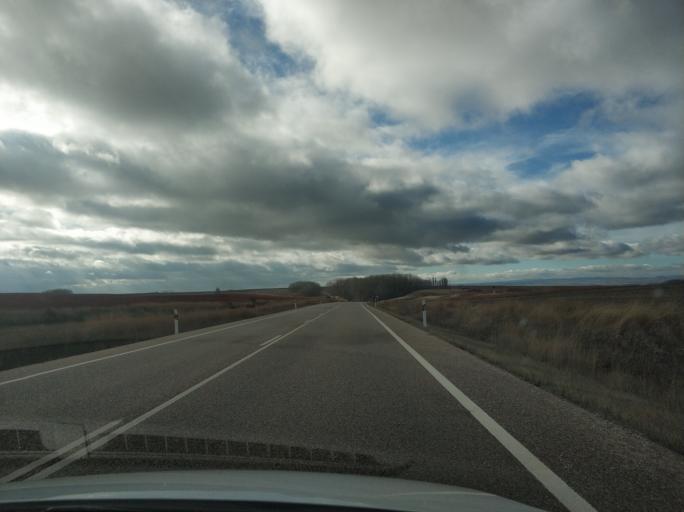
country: ES
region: Castille and Leon
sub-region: Provincia de Segovia
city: Ayllon
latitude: 41.4376
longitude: -3.3483
